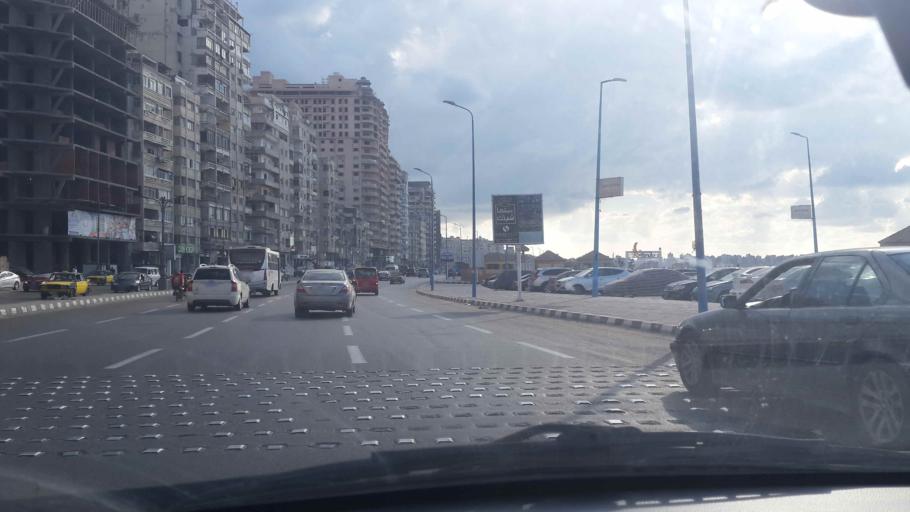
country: EG
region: Alexandria
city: Alexandria
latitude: 31.2162
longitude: 29.9231
